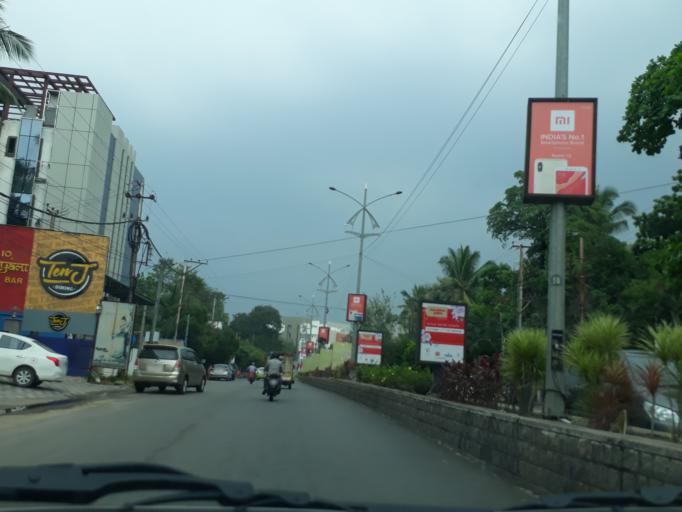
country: IN
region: Telangana
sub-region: Rangareddi
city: Kukatpalli
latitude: 17.4347
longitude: 78.4142
